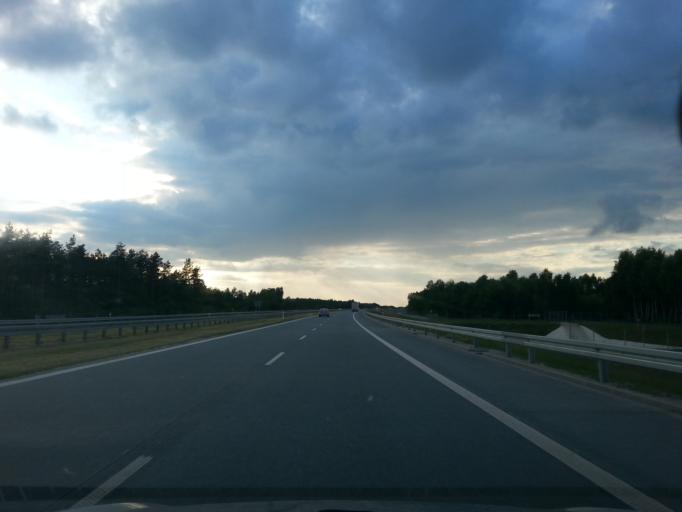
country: PL
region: Lodz Voivodeship
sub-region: Powiat zdunskowolski
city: Zdunska Wola
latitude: 51.5821
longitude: 18.9055
